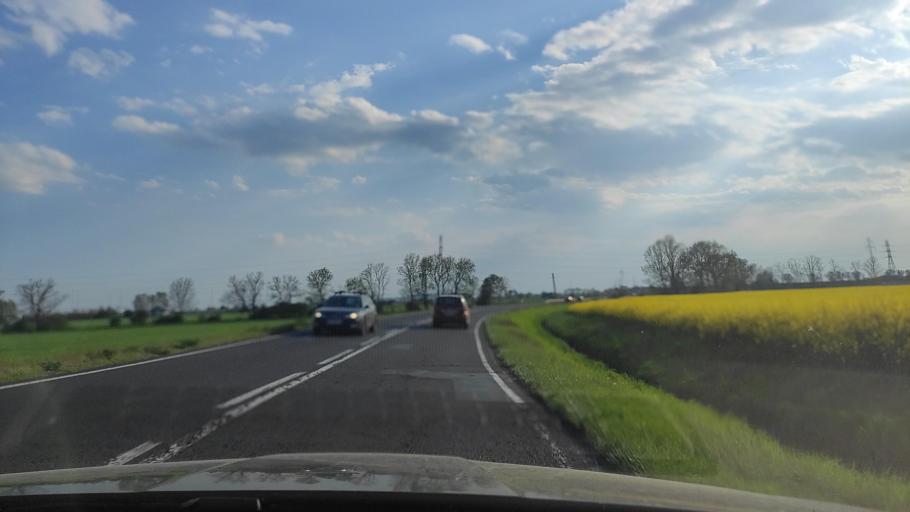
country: PL
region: Greater Poland Voivodeship
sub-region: Powiat poznanski
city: Kleszczewo
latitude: 52.3159
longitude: 17.1509
